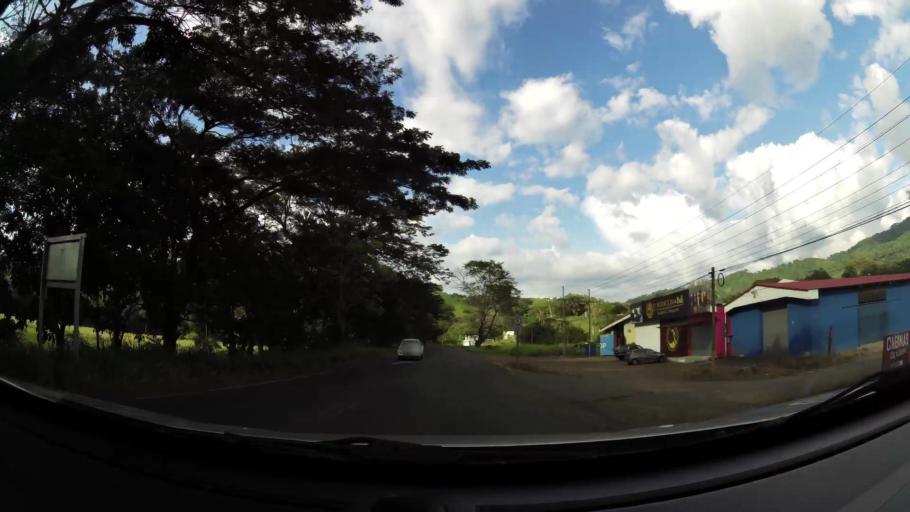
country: CR
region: Puntarenas
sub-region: Canton de Garabito
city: Jaco
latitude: 9.7182
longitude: -84.6320
